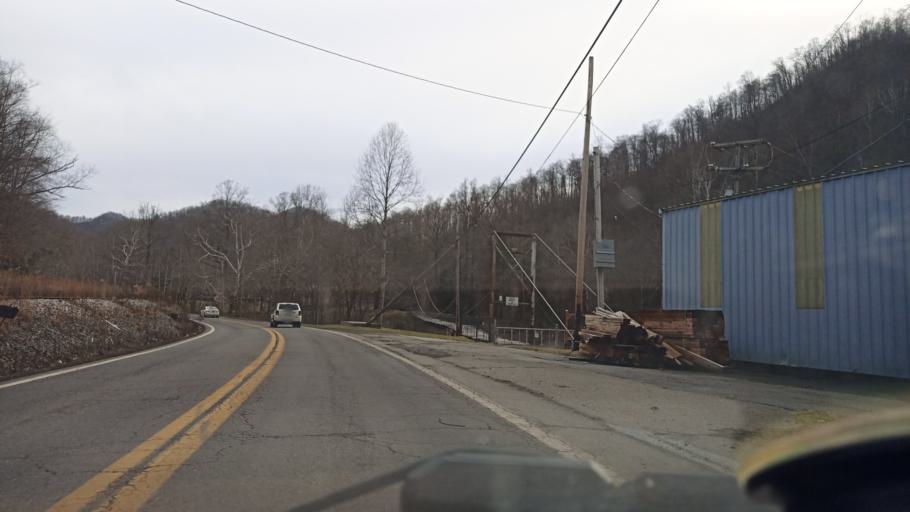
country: US
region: West Virginia
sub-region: Mingo County
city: Gilbert Creek
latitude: 37.6223
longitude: -81.8685
